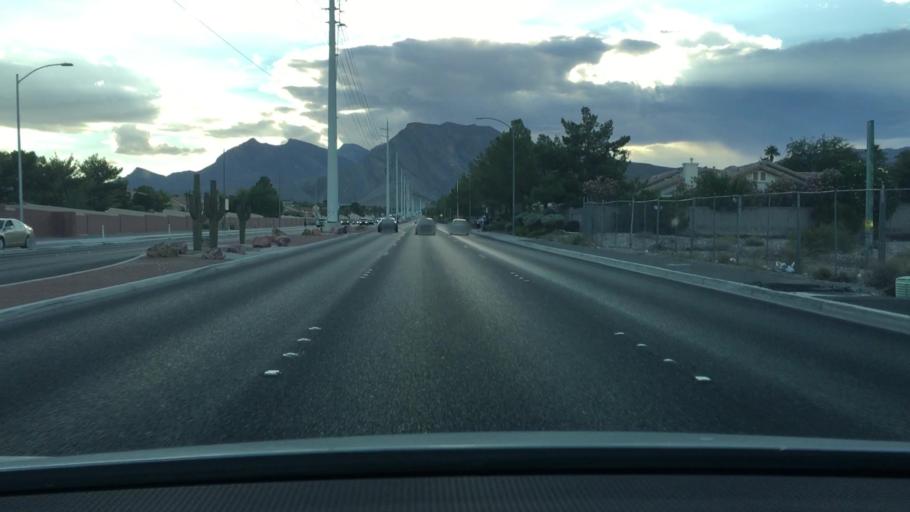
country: US
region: Nevada
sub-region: Clark County
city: Summerlin South
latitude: 36.2186
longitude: -115.2977
